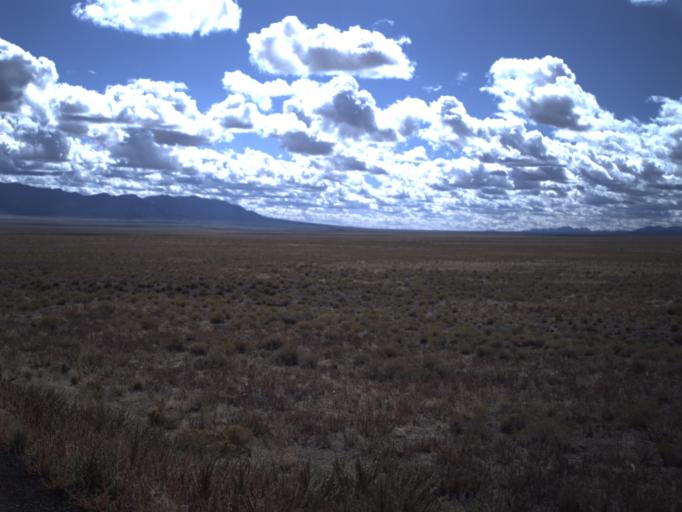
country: US
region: Utah
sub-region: Beaver County
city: Milford
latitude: 38.5777
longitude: -113.8034
